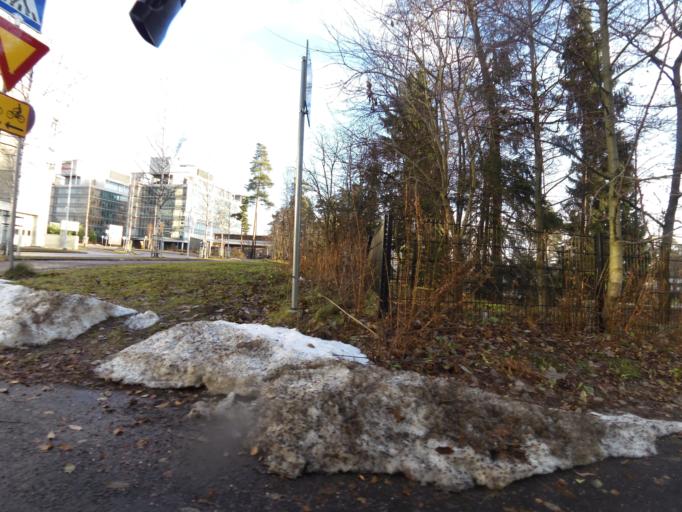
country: FI
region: Uusimaa
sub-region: Helsinki
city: Otaniemi
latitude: 60.1771
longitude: 24.8344
